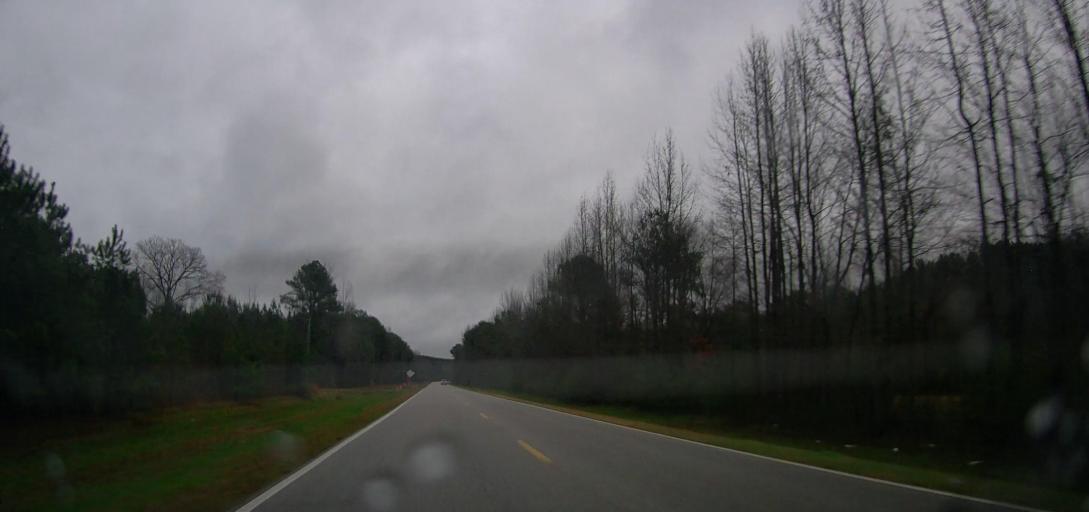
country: US
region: Alabama
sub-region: Bibb County
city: Centreville
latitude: 32.9237
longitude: -87.0400
